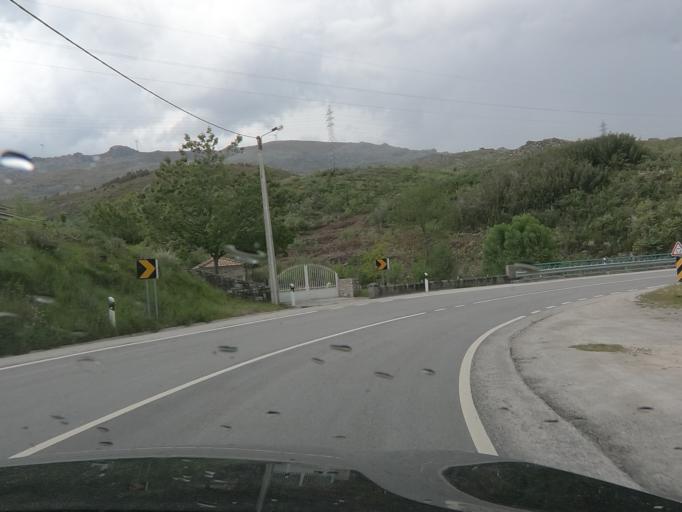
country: PT
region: Vila Real
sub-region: Vila Real
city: Vila Real
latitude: 41.3757
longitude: -7.7185
